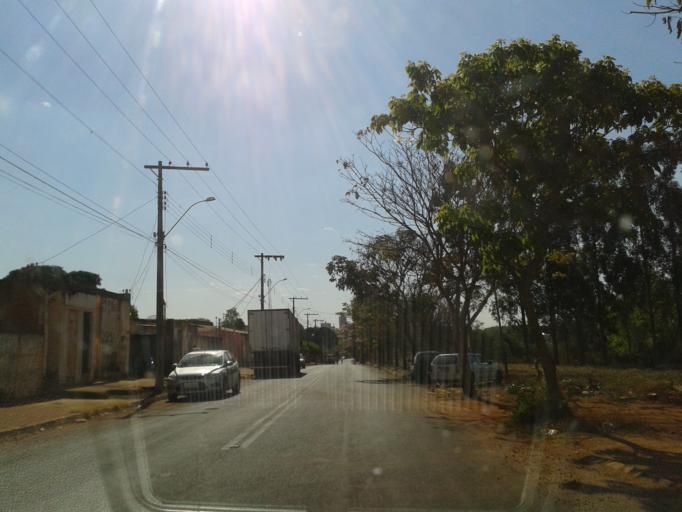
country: BR
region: Minas Gerais
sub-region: Araguari
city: Araguari
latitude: -18.6620
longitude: -48.1751
